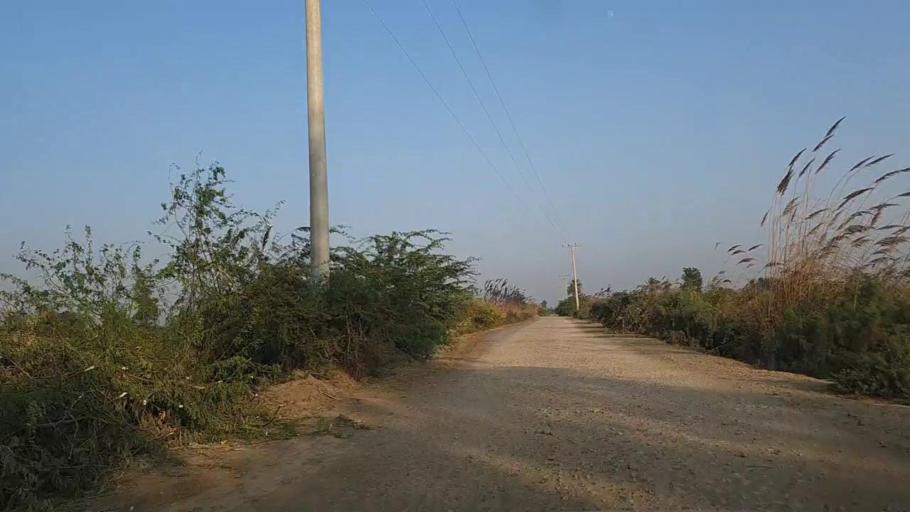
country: PK
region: Sindh
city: Keti Bandar
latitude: 24.2769
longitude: 67.6520
